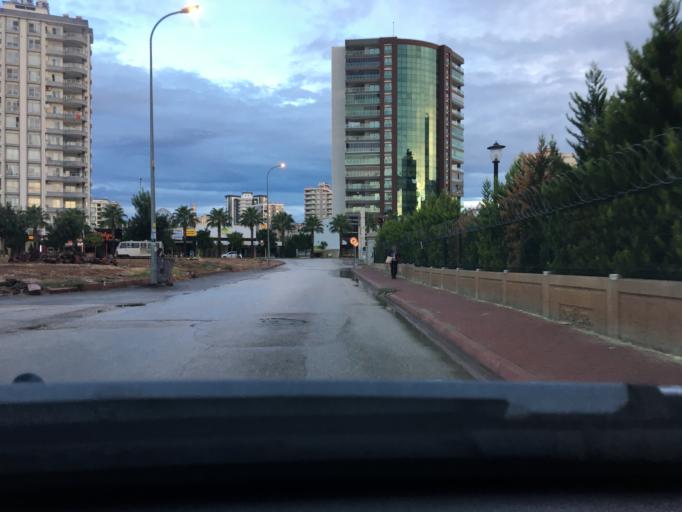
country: TR
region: Adana
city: Seyhan
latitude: 37.0215
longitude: 35.2789
